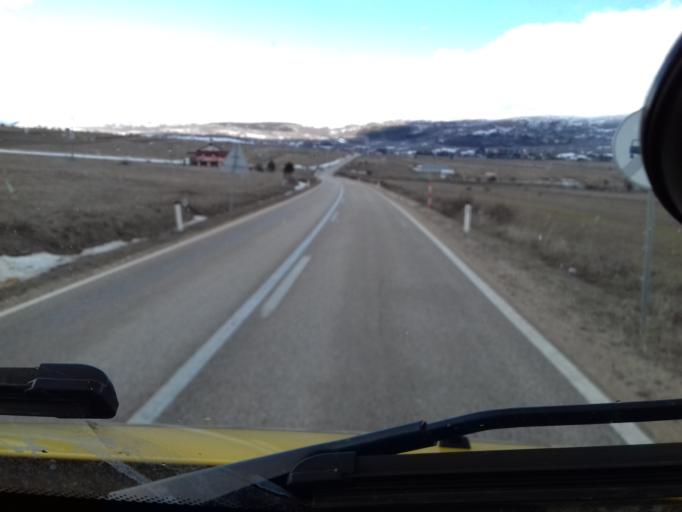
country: BA
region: Federation of Bosnia and Herzegovina
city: Tomislavgrad
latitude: 43.7381
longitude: 17.2237
